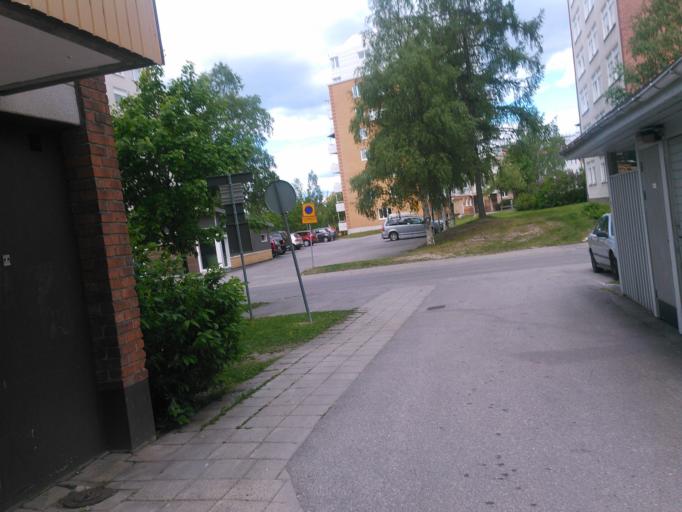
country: SE
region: Vaesterbotten
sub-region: Umea Kommun
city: Umea
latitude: 63.8132
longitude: 20.3000
